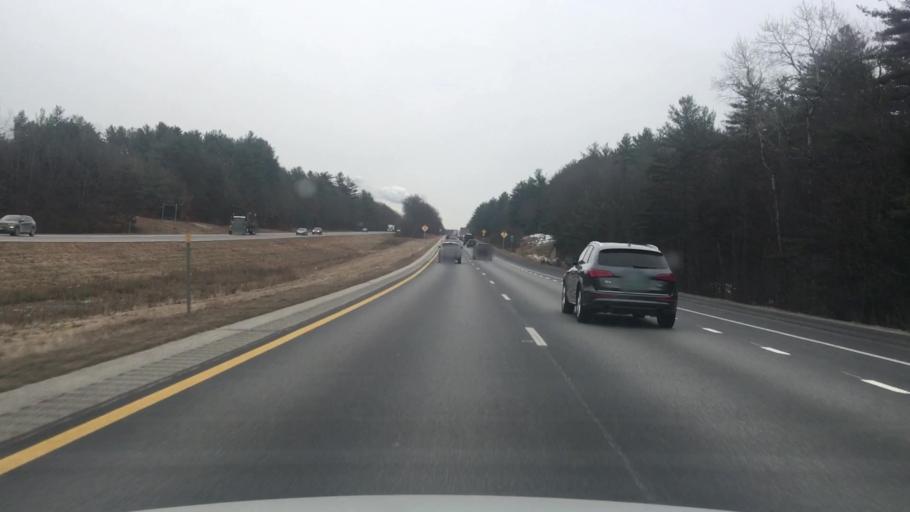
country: US
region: New Hampshire
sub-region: Merrimack County
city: Concord
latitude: 43.1765
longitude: -71.5606
